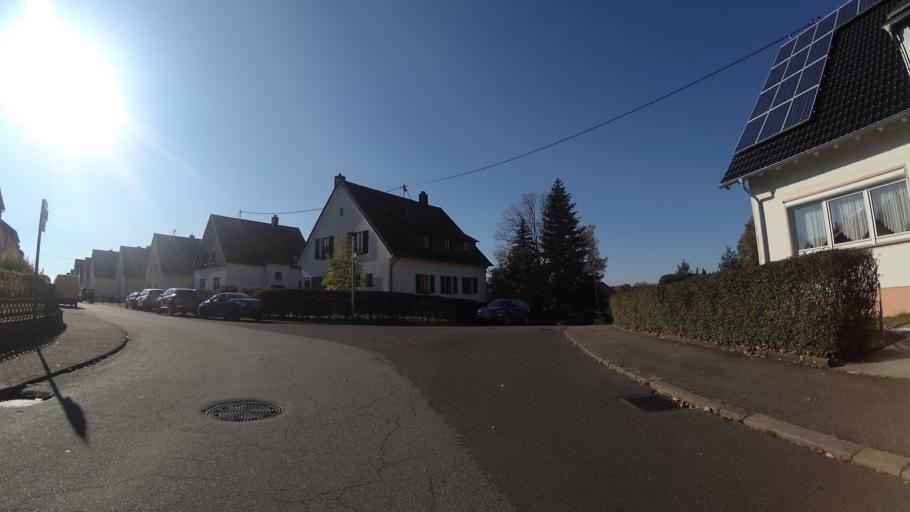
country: DE
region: Saarland
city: Neunkirchen
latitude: 49.3452
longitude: 7.1990
